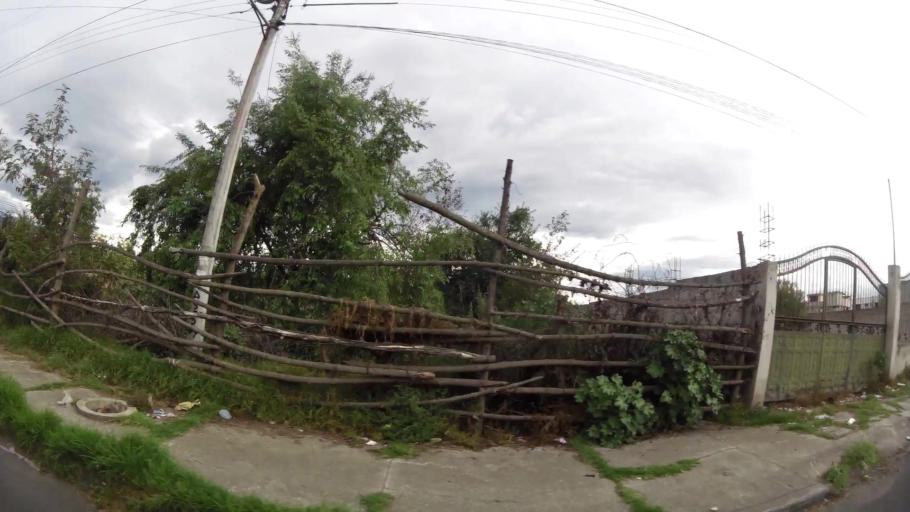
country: EC
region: Tungurahua
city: Ambato
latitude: -1.2777
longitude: -78.6215
